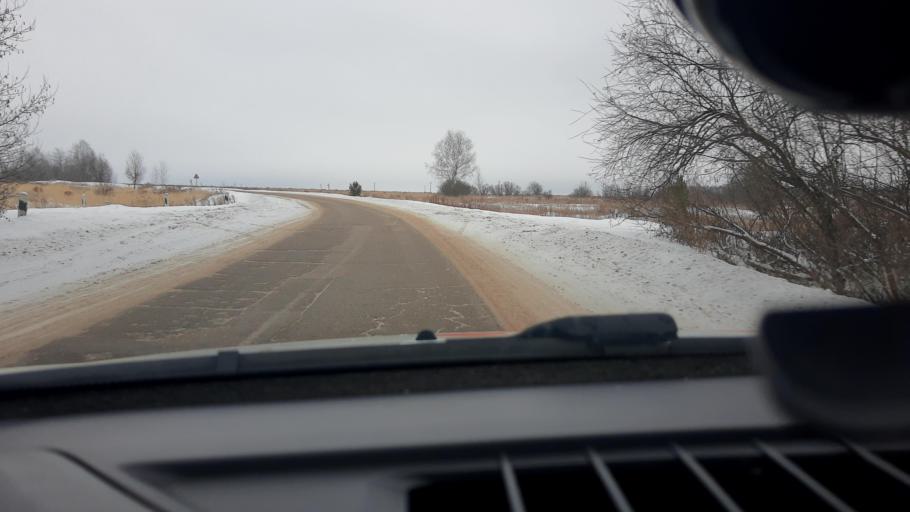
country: RU
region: Nizjnij Novgorod
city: Dal'neye Konstantinovo
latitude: 55.9314
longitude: 44.0101
